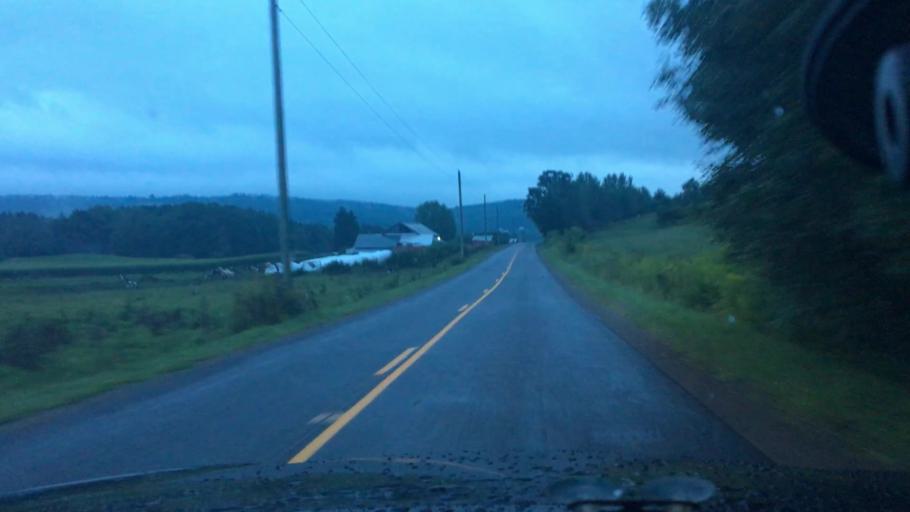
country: US
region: New York
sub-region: Cattaraugus County
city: Little Valley
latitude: 42.2428
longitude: -78.8898
